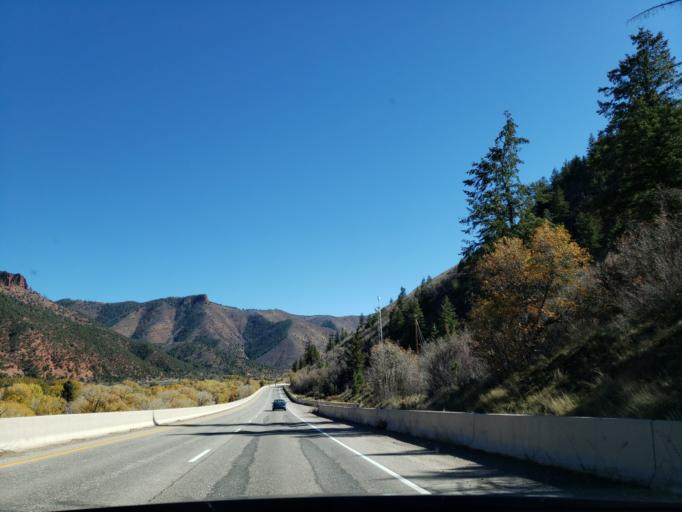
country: US
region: Colorado
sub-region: Eagle County
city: Basalt
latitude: 39.3282
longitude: -106.9641
